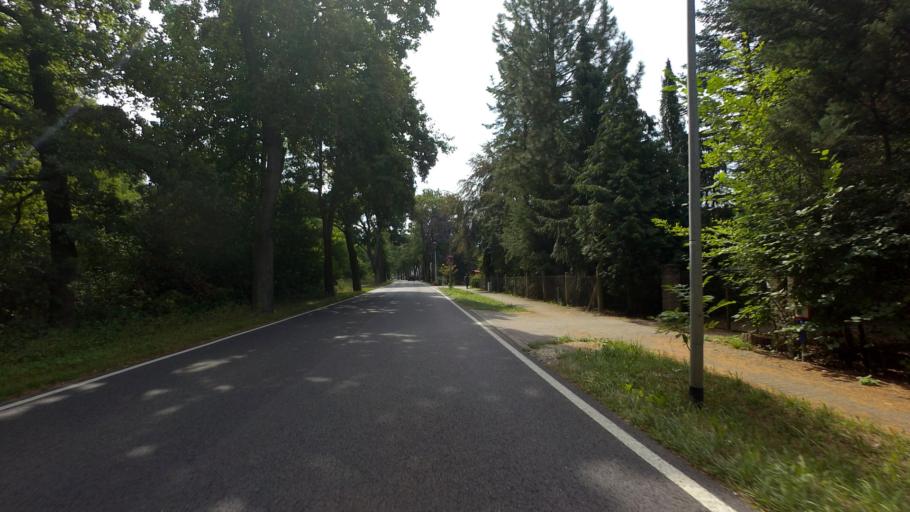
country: DE
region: Brandenburg
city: Mittenwalde
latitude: 52.2378
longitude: 13.5661
